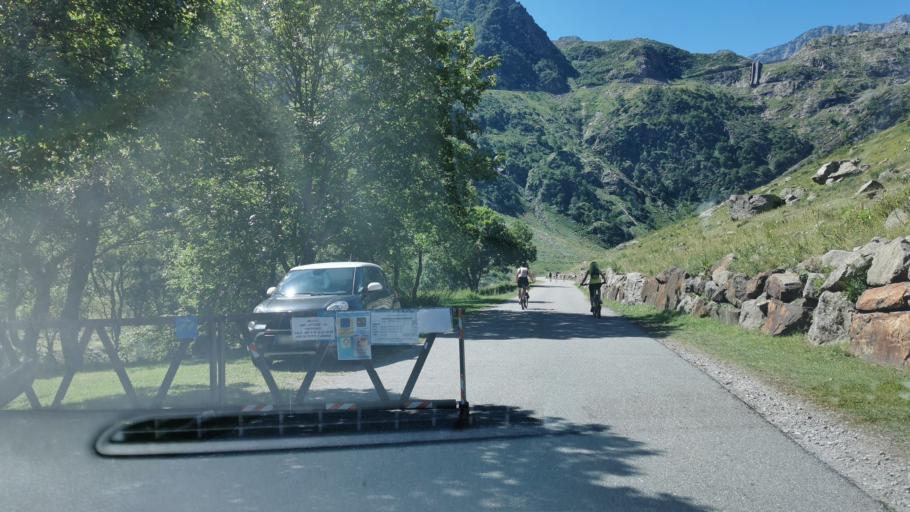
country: IT
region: Piedmont
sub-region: Provincia di Cuneo
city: Entracque
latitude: 44.1809
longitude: 7.3448
